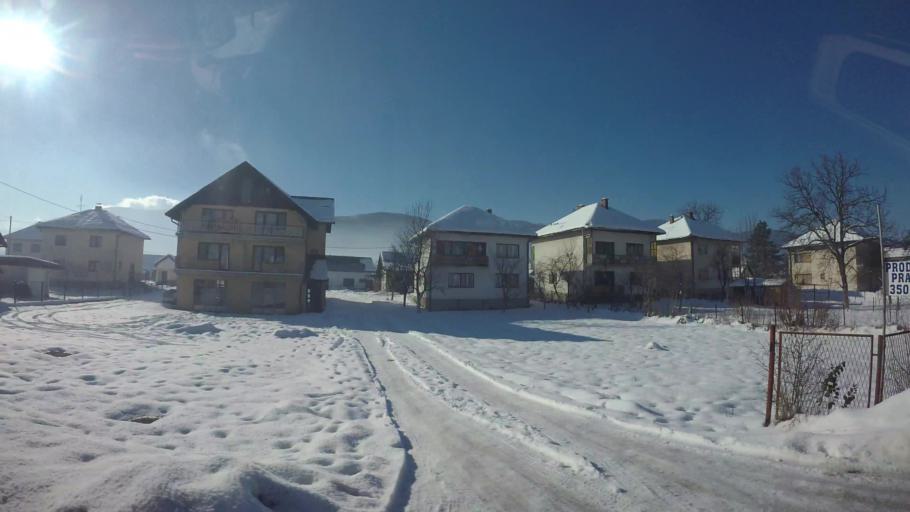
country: BA
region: Federation of Bosnia and Herzegovina
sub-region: Kanton Sarajevo
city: Sarajevo
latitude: 43.7969
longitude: 18.3509
